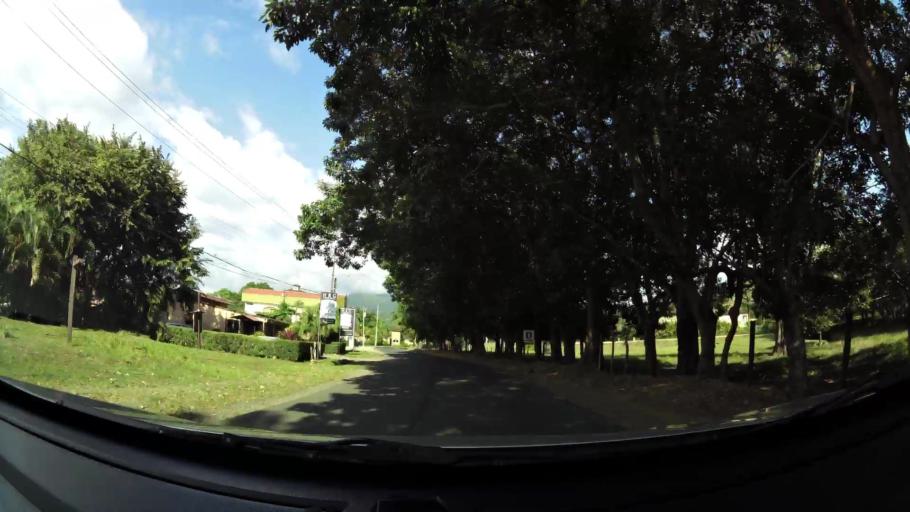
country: CR
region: Puntarenas
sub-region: Canton de Garabito
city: Jaco
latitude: 9.6560
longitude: -84.6458
